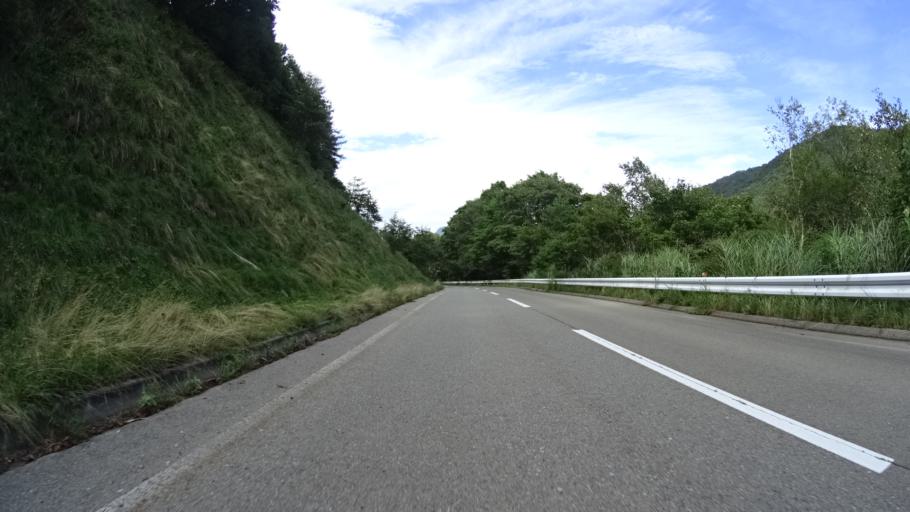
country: JP
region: Yamanashi
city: Nirasaki
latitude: 35.9186
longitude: 138.5418
